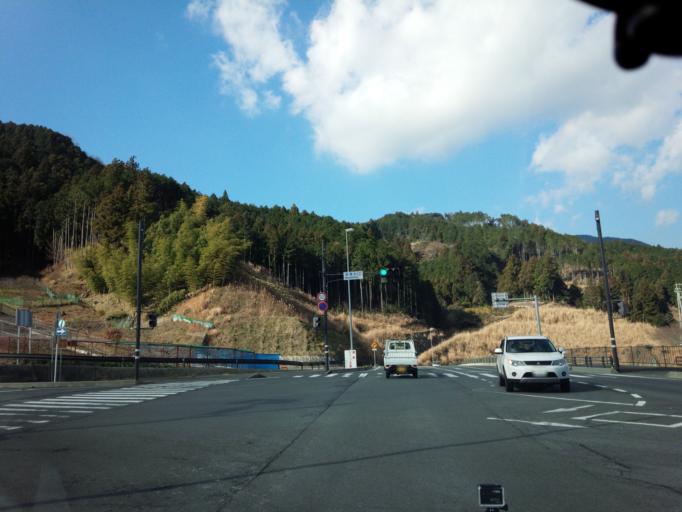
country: JP
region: Shizuoka
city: Fujinomiya
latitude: 35.1512
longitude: 138.5211
